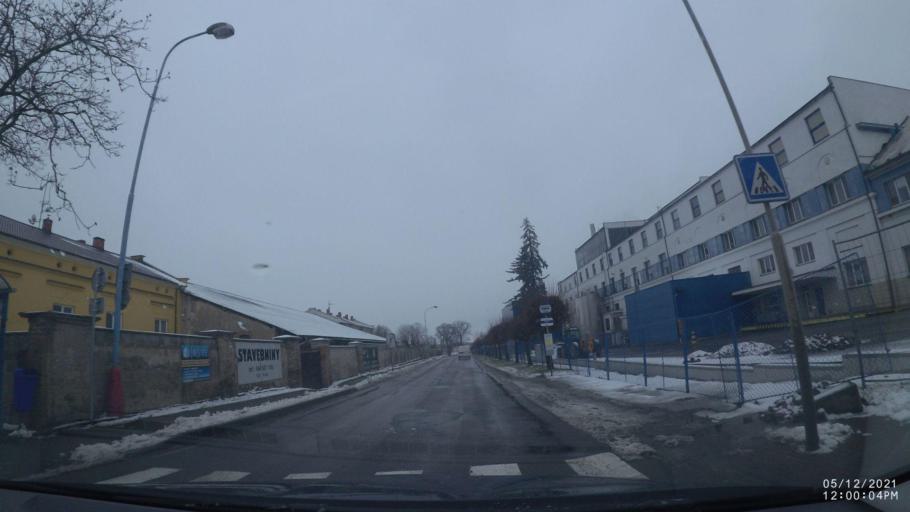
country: CZ
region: Kralovehradecky
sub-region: Okres Rychnov nad Kneznou
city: Opocno
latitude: 50.2756
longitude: 16.0927
